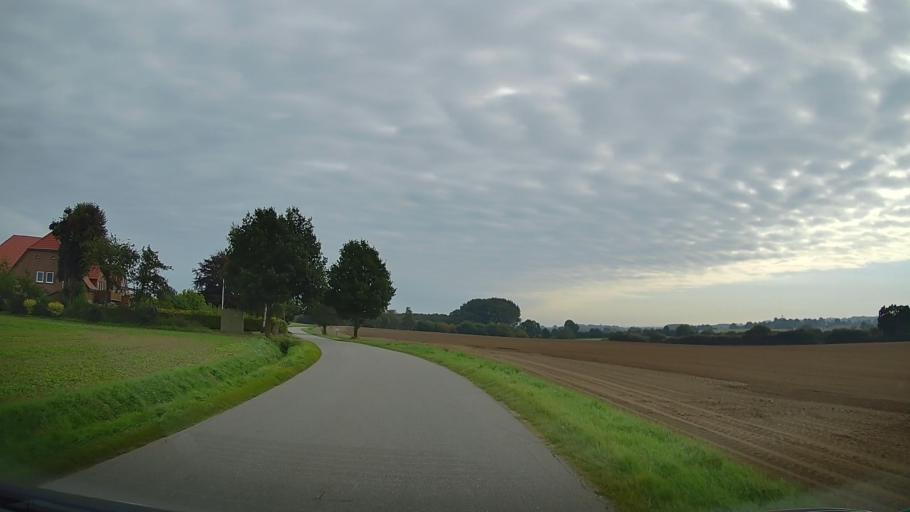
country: DE
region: Schleswig-Holstein
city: Panker
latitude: 54.3582
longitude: 10.5551
